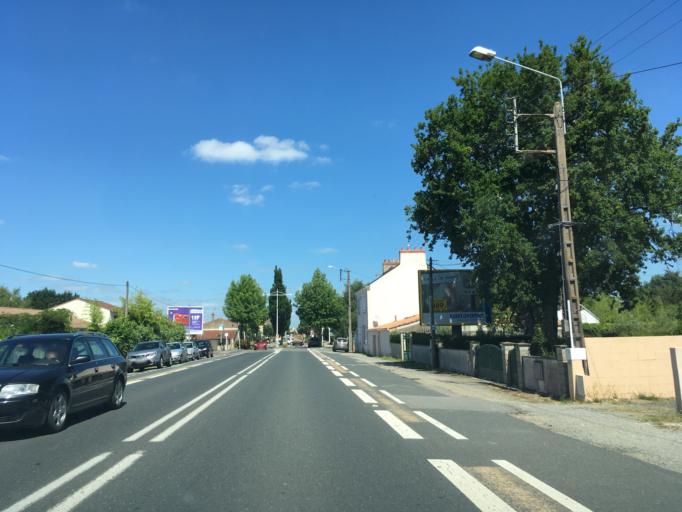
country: FR
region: Pays de la Loire
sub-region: Departement de la Loire-Atlantique
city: Les Sorinieres
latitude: 47.1450
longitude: -1.5270
